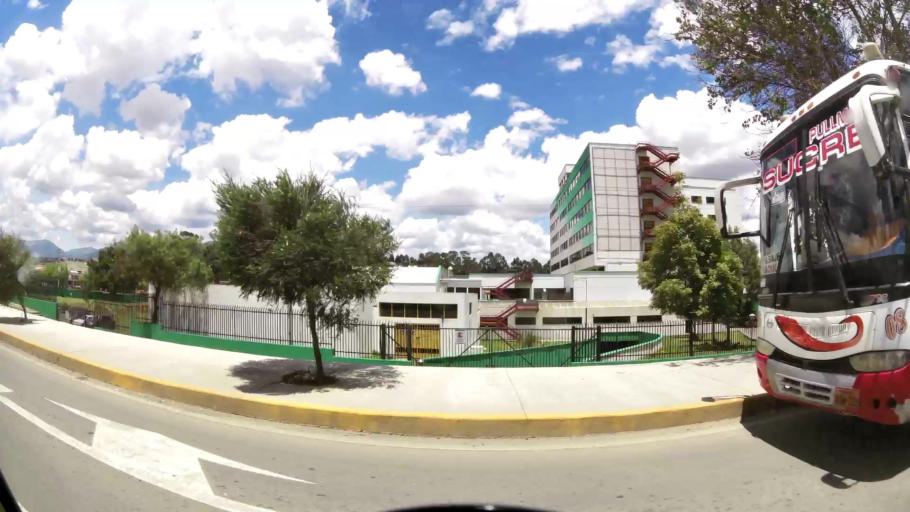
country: EC
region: Azuay
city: Cuenca
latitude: -2.8998
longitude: -78.9704
